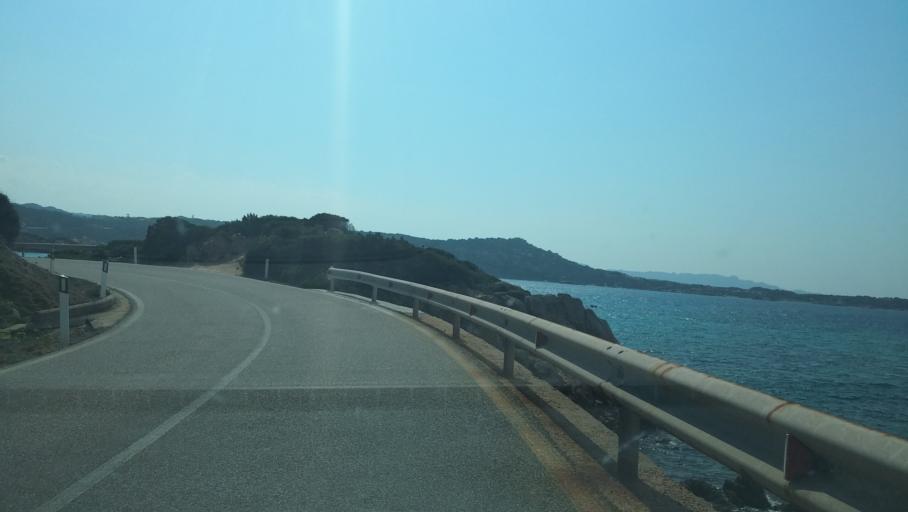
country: IT
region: Sardinia
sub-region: Provincia di Olbia-Tempio
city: La Maddalena
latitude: 41.2559
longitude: 9.4157
